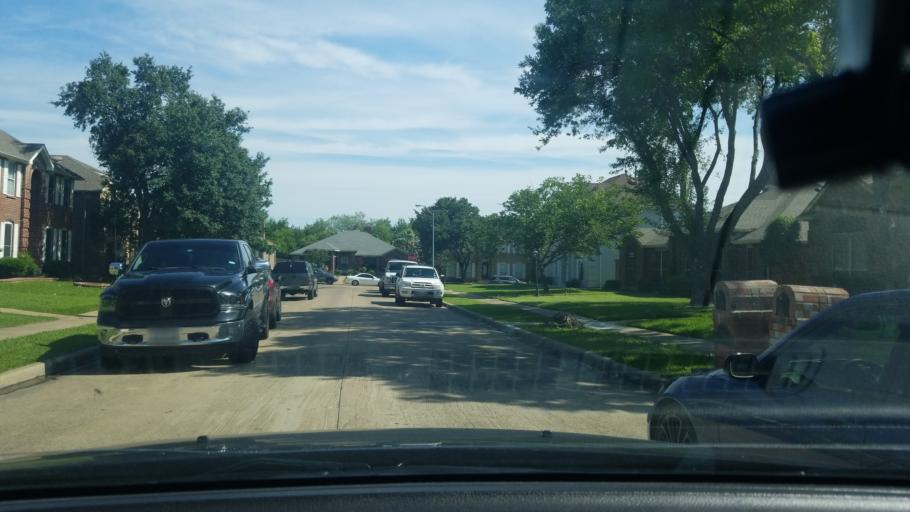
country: US
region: Texas
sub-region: Dallas County
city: Mesquite
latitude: 32.7769
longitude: -96.5907
